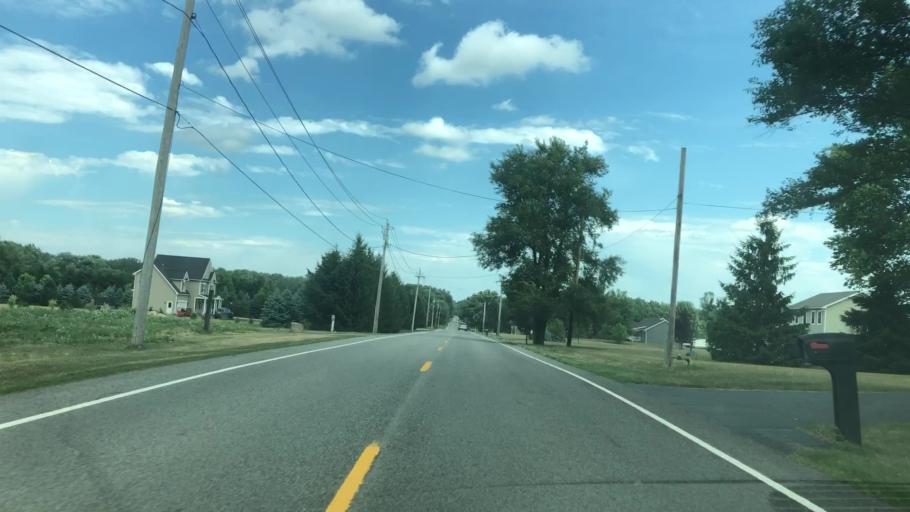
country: US
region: New York
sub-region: Wayne County
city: Macedon
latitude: 43.1095
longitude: -77.3523
